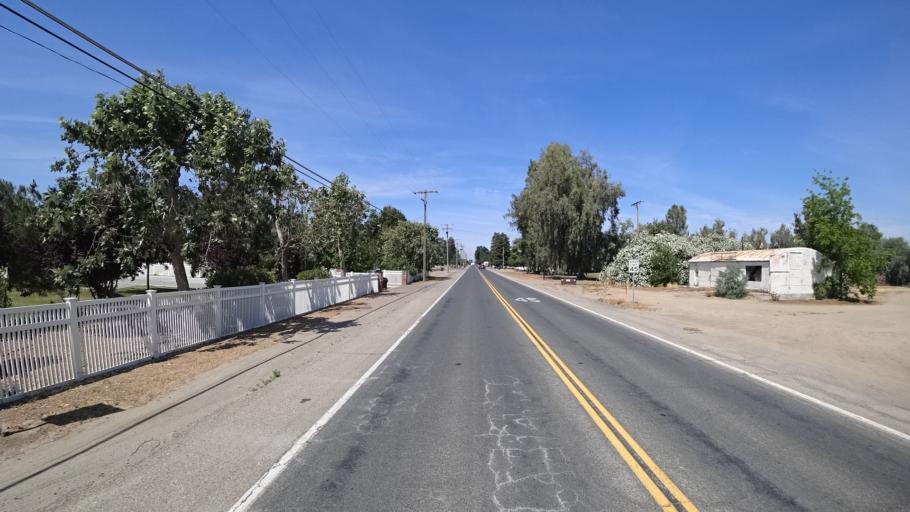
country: US
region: California
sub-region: Kings County
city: Armona
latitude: 36.3426
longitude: -119.7030
